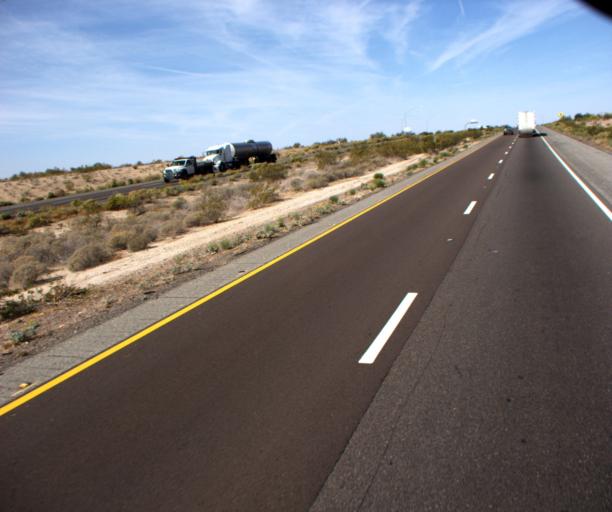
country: US
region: Arizona
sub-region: Maricopa County
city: Buckeye
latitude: 33.4282
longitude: -112.6277
